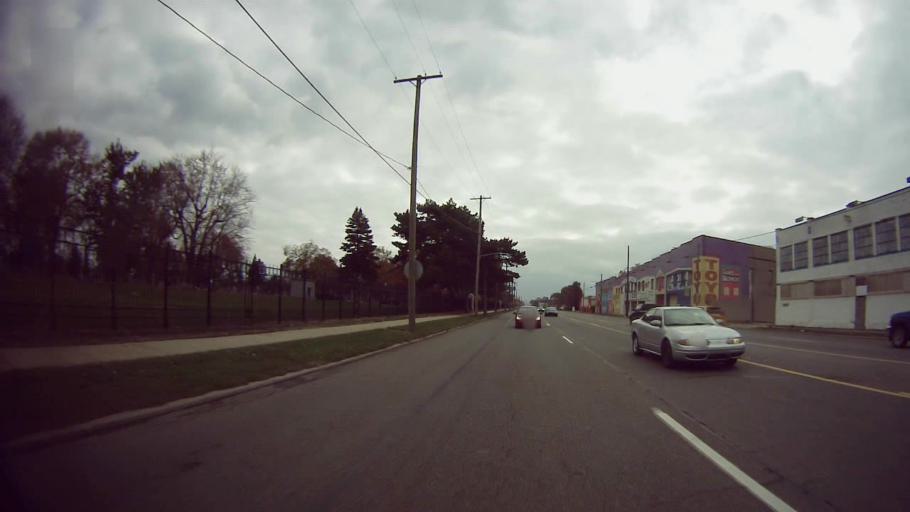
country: US
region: Michigan
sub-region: Wayne County
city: Hamtramck
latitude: 42.4232
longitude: -83.0237
